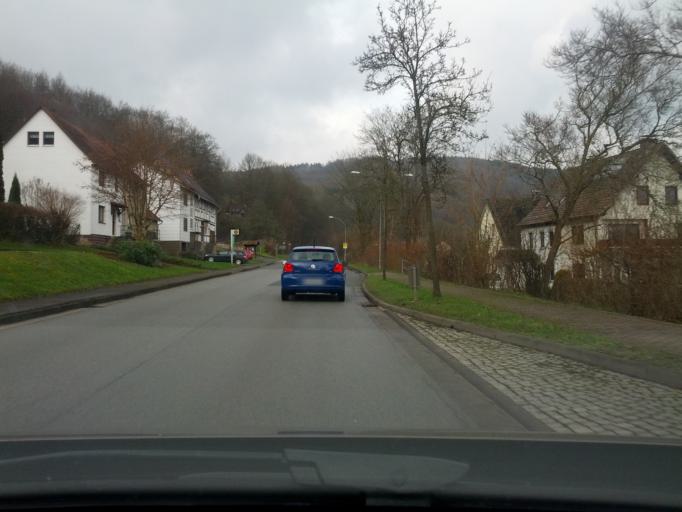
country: DE
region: Lower Saxony
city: Bodenfelde
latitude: 51.5982
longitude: 9.5445
